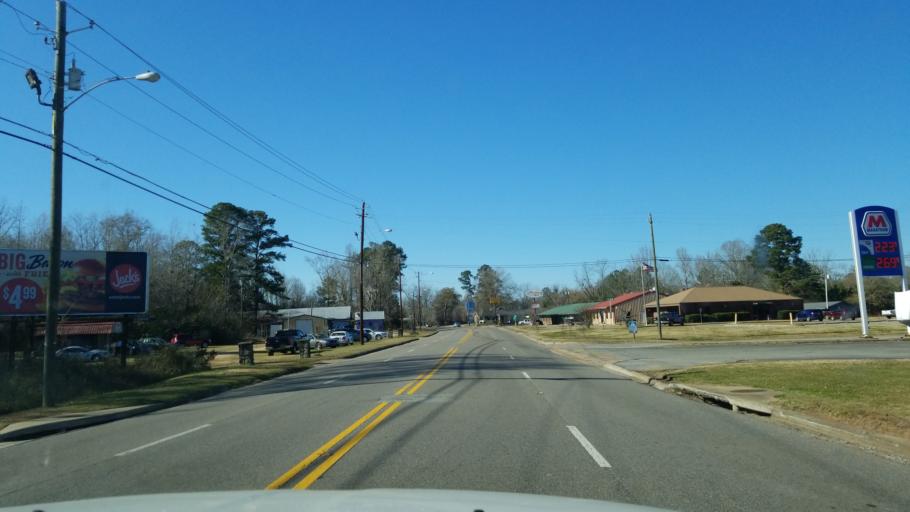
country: US
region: Alabama
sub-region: Pickens County
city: Reform
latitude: 33.3770
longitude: -88.0101
